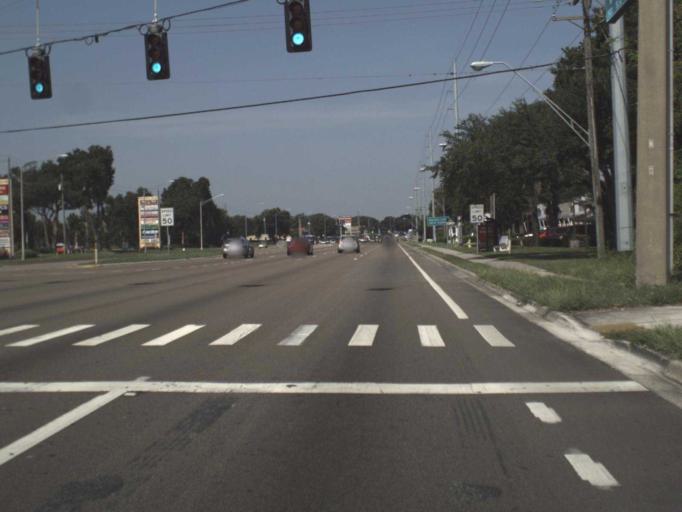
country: US
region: Florida
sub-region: Hillsborough County
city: Brandon
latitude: 27.9378
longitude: -82.3141
